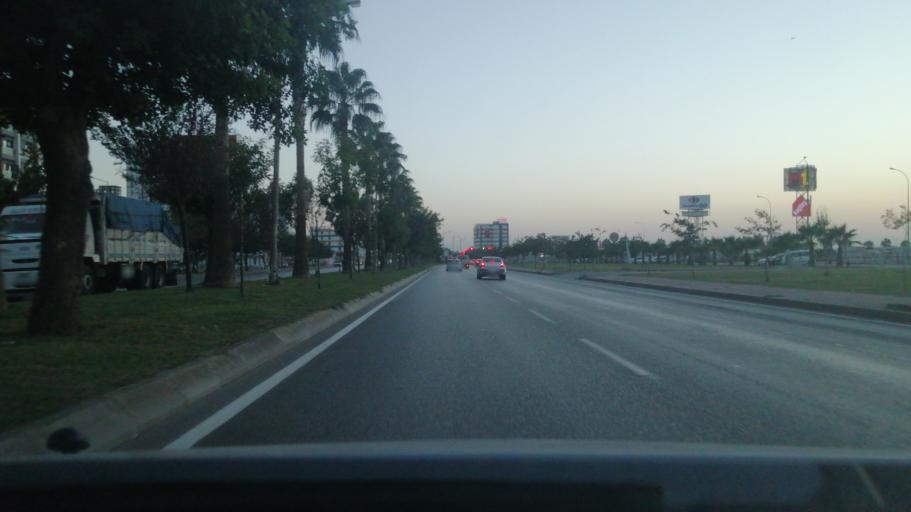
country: TR
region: Adana
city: Seyhan
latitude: 37.0185
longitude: 35.2519
